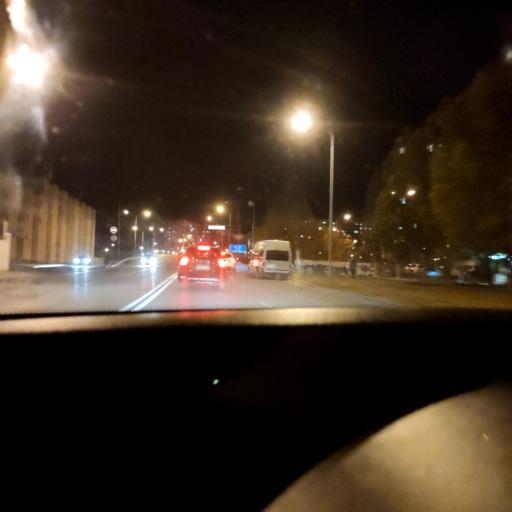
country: RU
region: Samara
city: Samara
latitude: 53.2699
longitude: 50.2188
